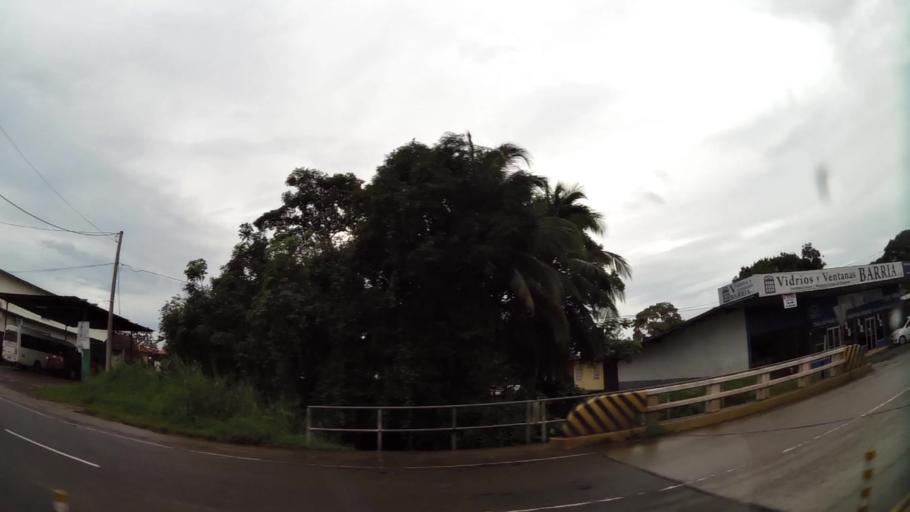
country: PA
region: Veraguas
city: Santiago de Veraguas
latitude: 8.1067
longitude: -80.9725
